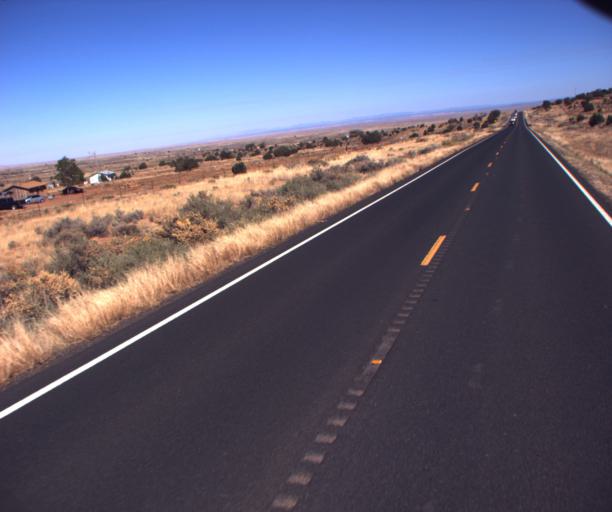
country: US
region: Arizona
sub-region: Apache County
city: Ganado
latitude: 35.7736
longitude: -109.7363
